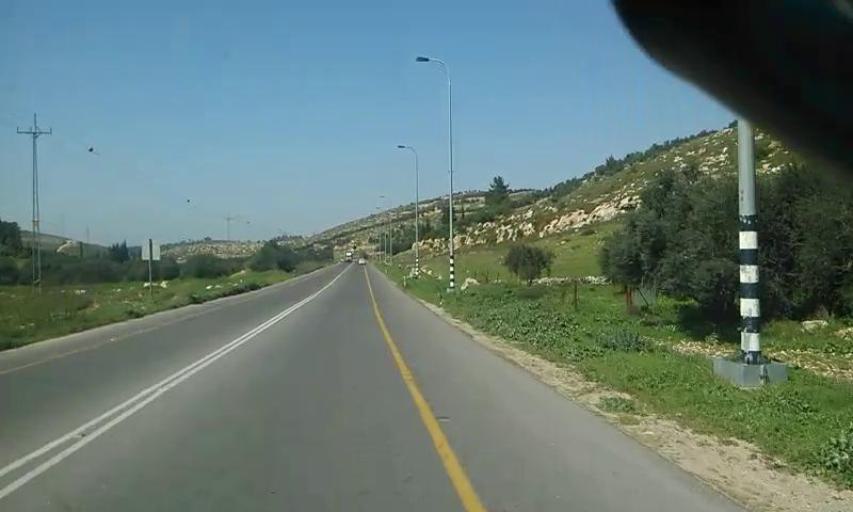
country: PS
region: West Bank
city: Idhna
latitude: 31.5762
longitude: 34.9807
